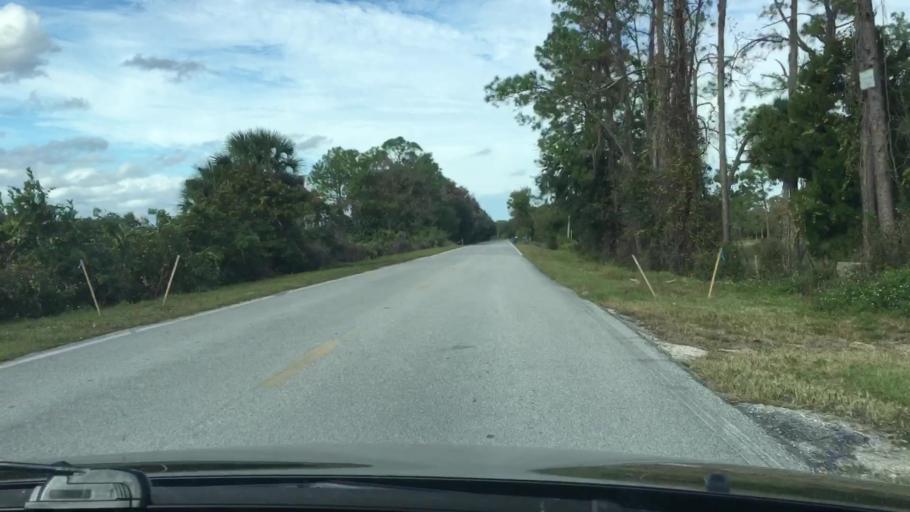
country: US
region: Florida
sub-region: Volusia County
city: Ormond Beach
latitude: 29.2955
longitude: -81.1288
